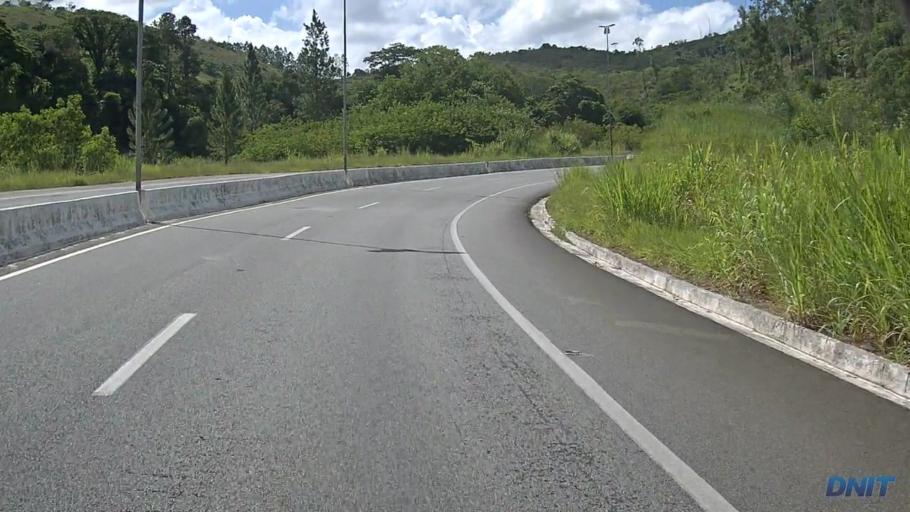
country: BR
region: Minas Gerais
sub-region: Nova Era
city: Nova Era
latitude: -19.7631
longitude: -43.0479
